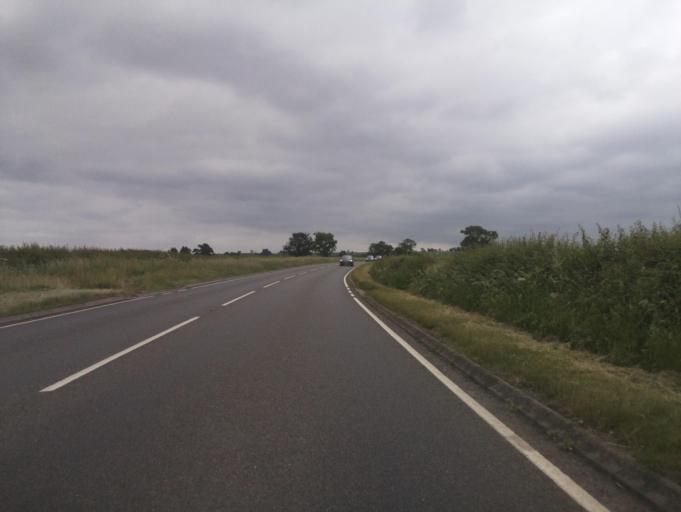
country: GB
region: England
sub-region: Leicestershire
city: Melton Mowbray
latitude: 52.7325
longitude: -0.8485
